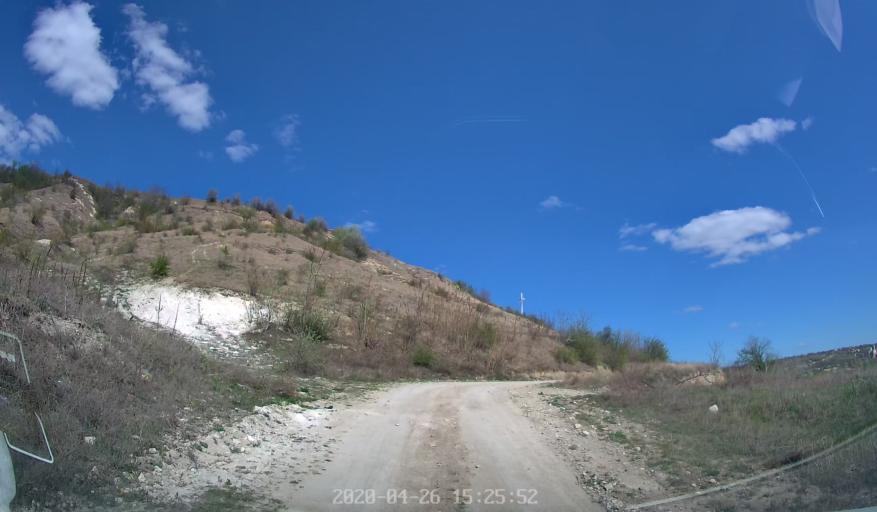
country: MD
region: Telenesti
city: Cocieri
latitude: 47.3650
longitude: 29.0905
